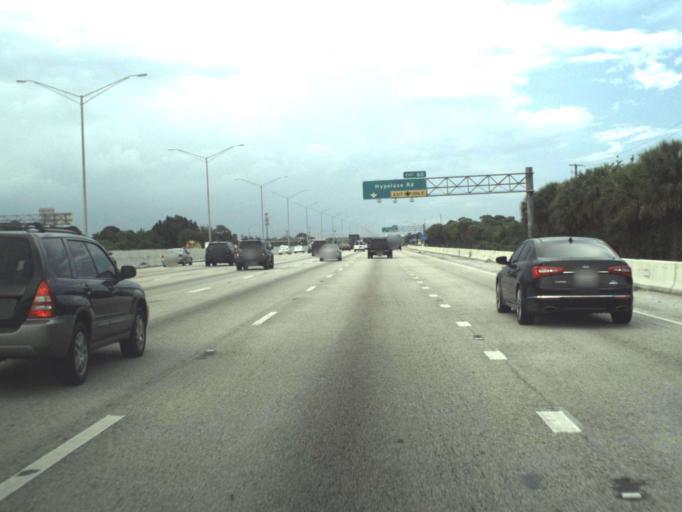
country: US
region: Florida
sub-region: Palm Beach County
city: Hypoluxo
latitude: 26.5646
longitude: -80.0695
